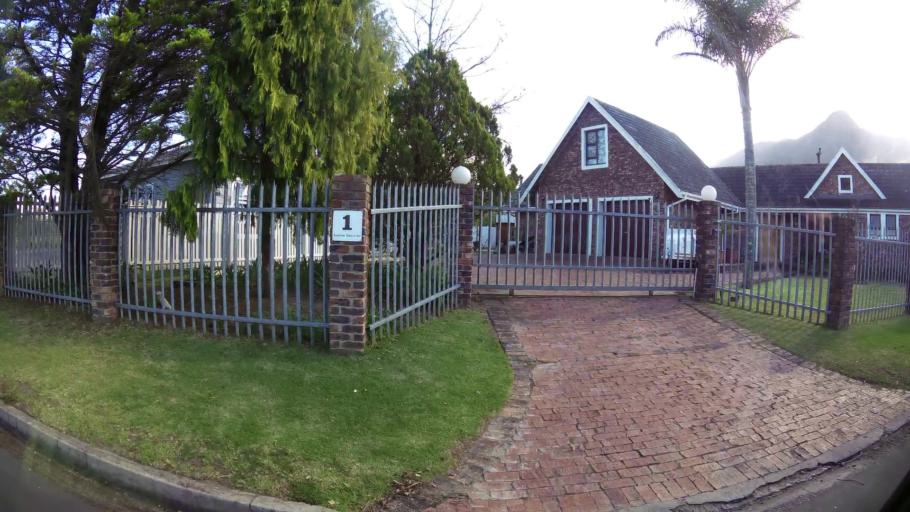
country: ZA
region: Western Cape
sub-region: Eden District Municipality
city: George
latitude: -33.9443
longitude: 22.4647
